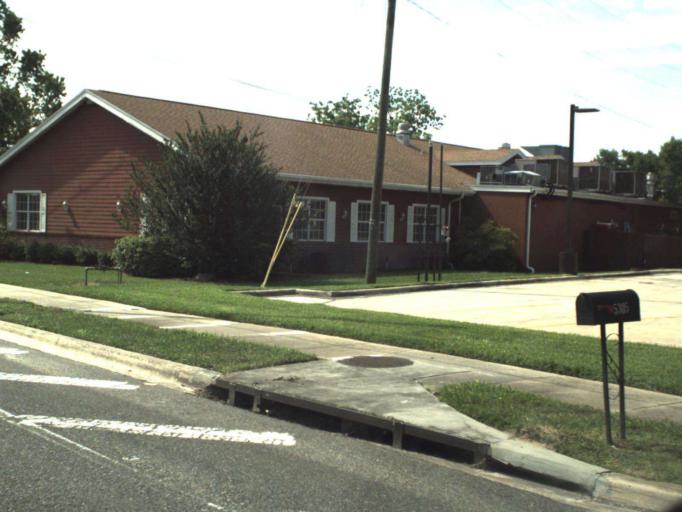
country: US
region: Florida
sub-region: Marion County
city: Belleview
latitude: 29.0604
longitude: -82.0612
